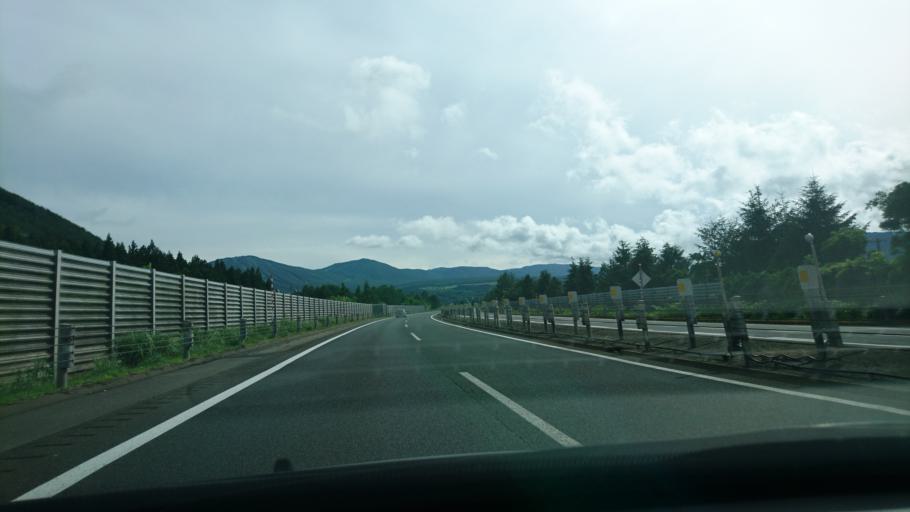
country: JP
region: Akita
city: Hanawa
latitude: 40.0355
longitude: 140.9890
